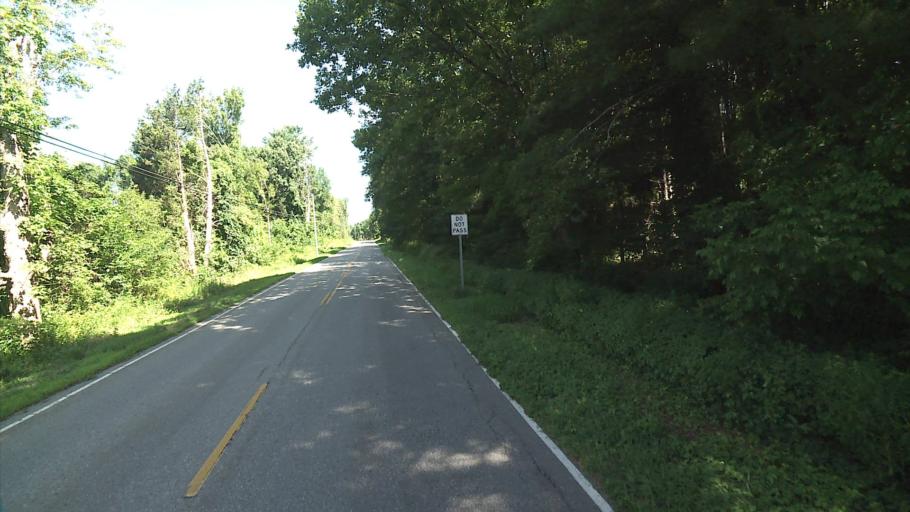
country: US
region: Connecticut
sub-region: New London County
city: Baltic
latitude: 41.6528
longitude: -72.0926
